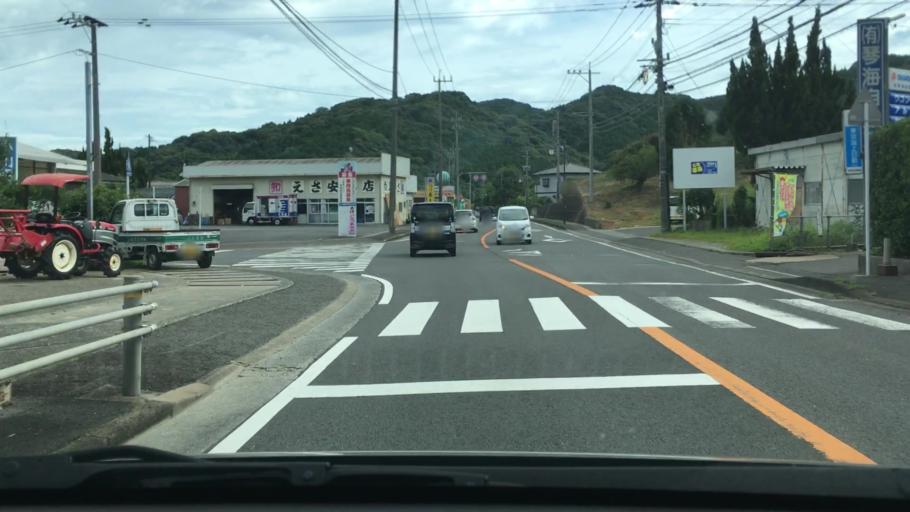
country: JP
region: Nagasaki
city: Togitsu
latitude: 32.8969
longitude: 129.7807
